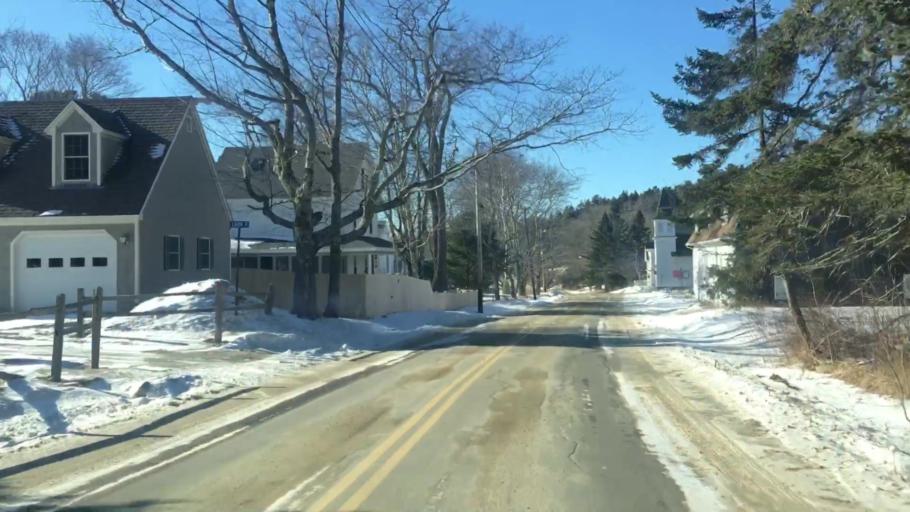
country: US
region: Maine
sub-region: Hancock County
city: Castine
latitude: 44.3416
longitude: -68.7375
